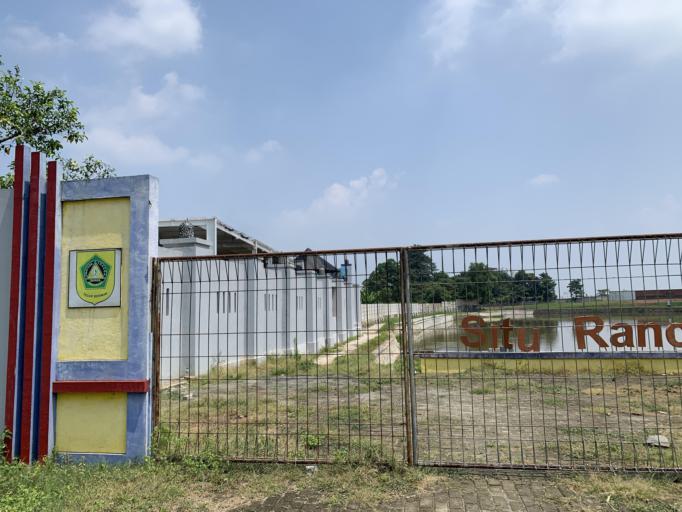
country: ID
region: Banten
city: Curug
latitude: -6.3781
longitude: 106.5442
